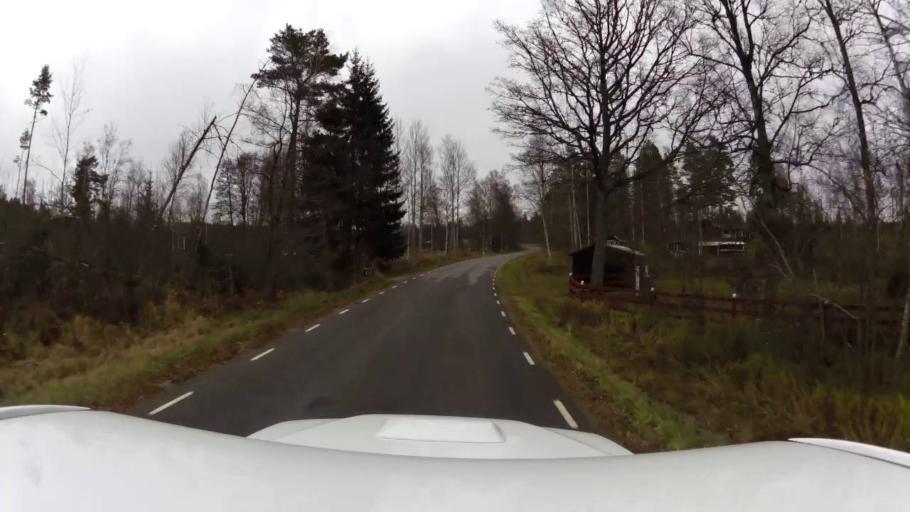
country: SE
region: OEstergoetland
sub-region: Kinda Kommun
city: Kisa
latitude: 58.1284
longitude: 15.4495
